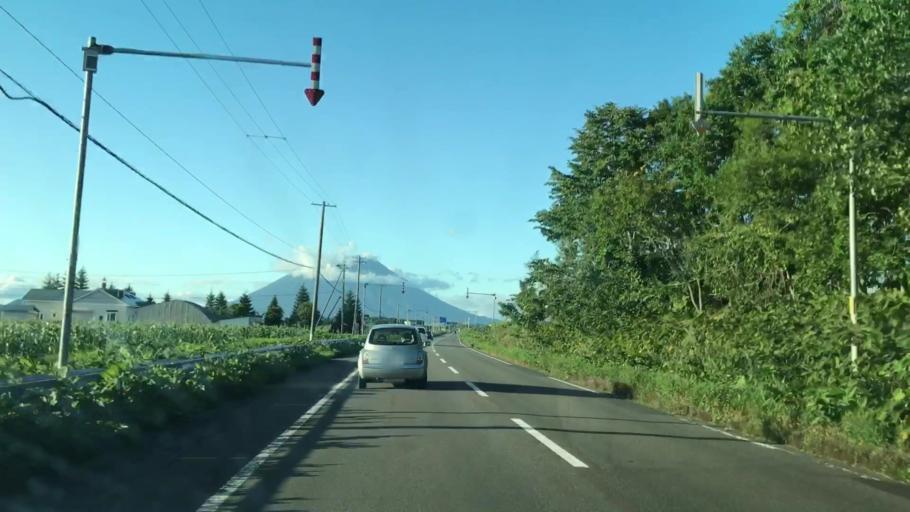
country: JP
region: Hokkaido
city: Niseko Town
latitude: 42.6560
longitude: 140.8112
